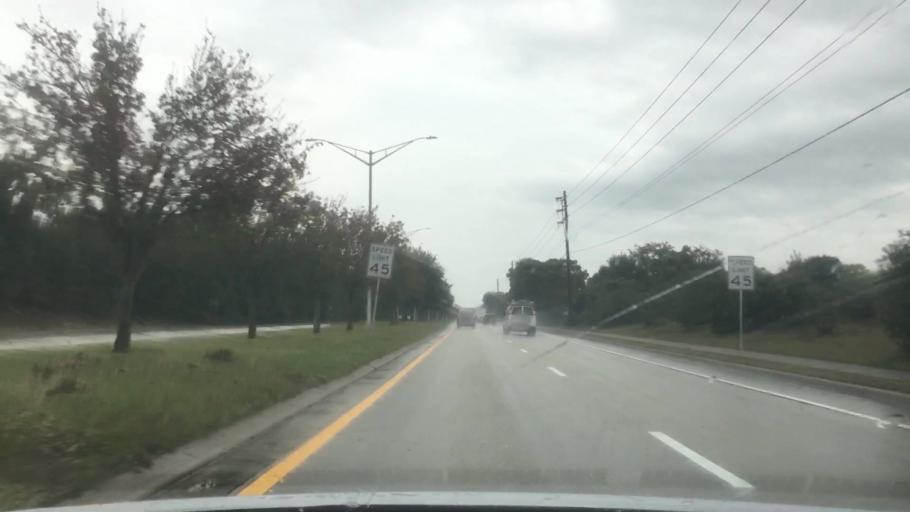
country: US
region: Florida
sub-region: Duval County
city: Atlantic Beach
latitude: 30.3480
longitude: -81.5229
